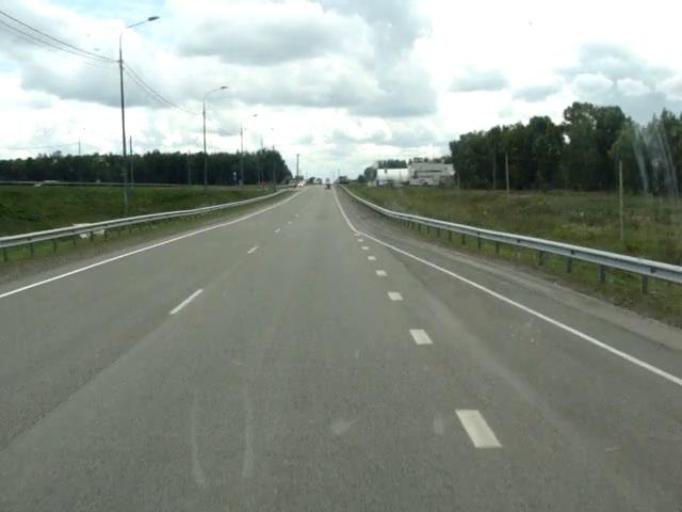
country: RU
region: Altai Krai
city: Zarya
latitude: 52.5782
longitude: 85.1778
